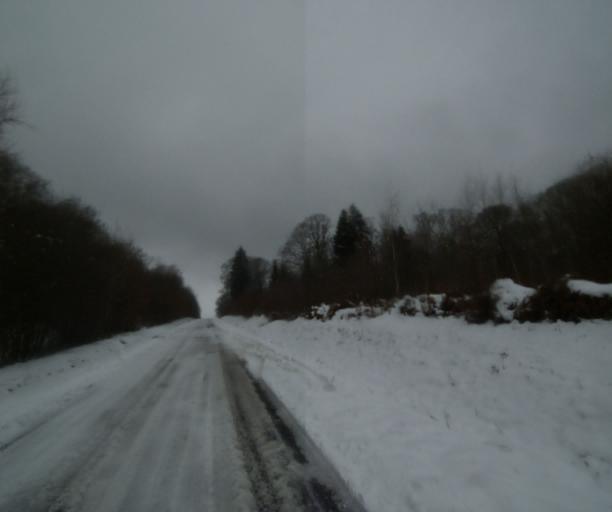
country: FR
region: Champagne-Ardenne
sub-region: Departement de la Haute-Marne
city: Wassy
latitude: 48.5134
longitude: 4.9135
